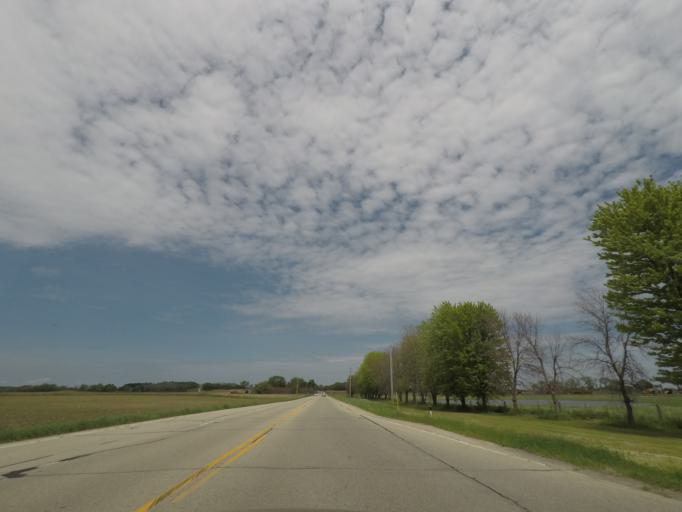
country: US
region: Wisconsin
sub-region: Rock County
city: Evansville
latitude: 42.8097
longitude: -89.2991
